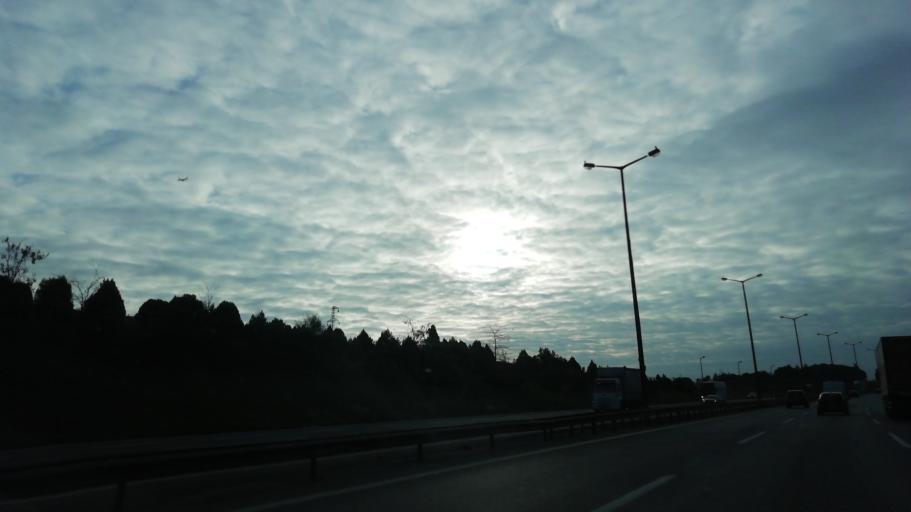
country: TR
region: Istanbul
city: Sultanbeyli
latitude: 40.9257
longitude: 29.3498
